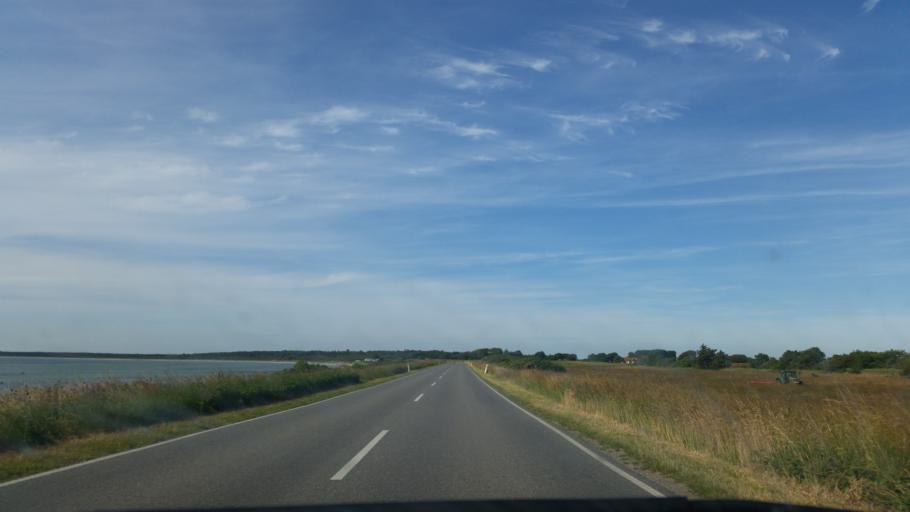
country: DK
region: Central Jutland
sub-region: Samso Kommune
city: Tranebjerg
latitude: 55.8981
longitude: 10.5980
